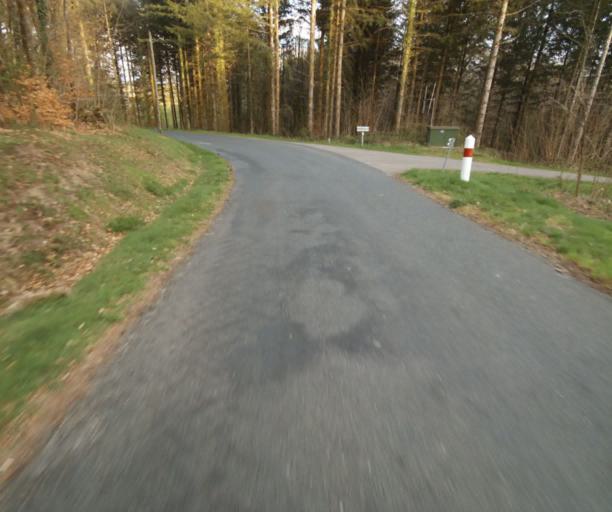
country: FR
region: Limousin
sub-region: Departement de la Correze
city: Argentat
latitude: 45.2394
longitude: 1.9669
